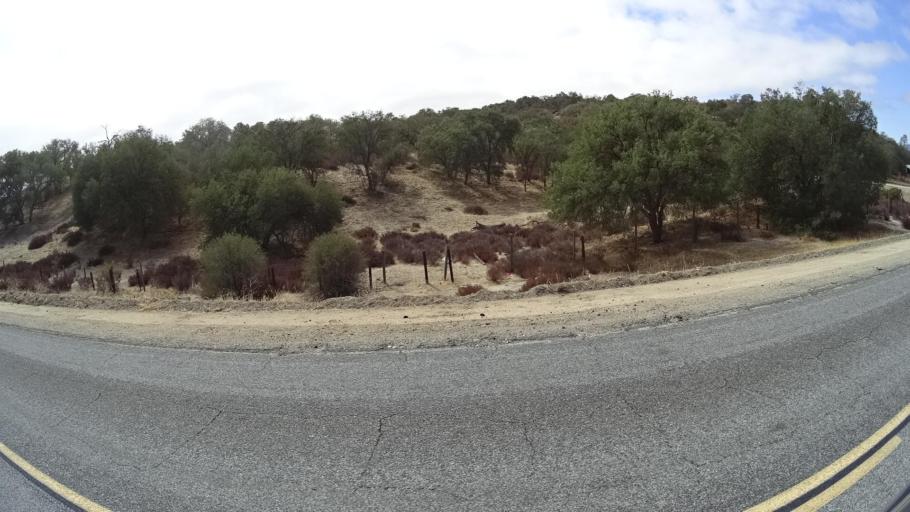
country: US
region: California
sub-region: San Luis Obispo County
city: Lake Nacimiento
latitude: 35.9084
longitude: -121.0051
